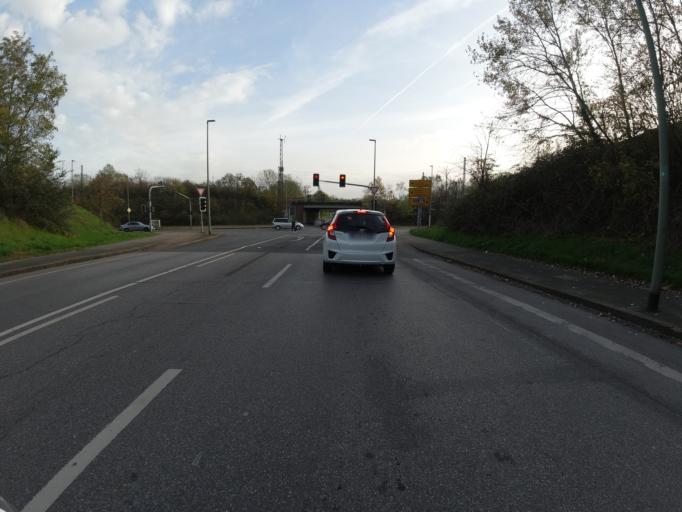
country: DE
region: North Rhine-Westphalia
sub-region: Regierungsbezirk Dusseldorf
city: Hochfeld
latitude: 51.3926
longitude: 6.7024
